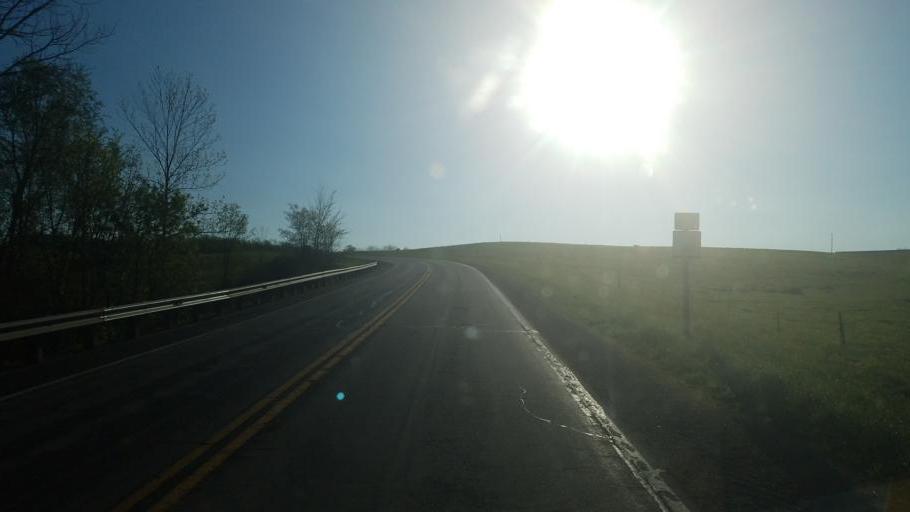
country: US
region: Wisconsin
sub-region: Vernon County
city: Hillsboro
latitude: 43.5922
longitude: -90.5103
